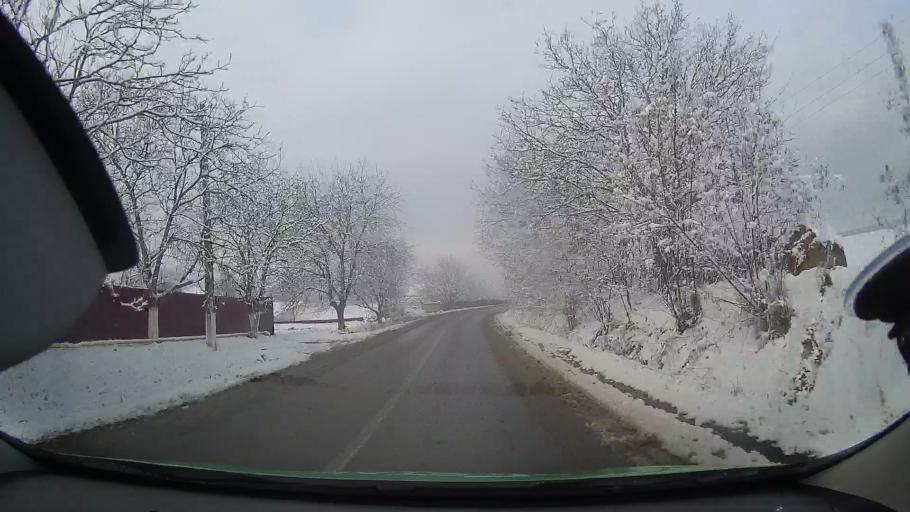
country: RO
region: Mures
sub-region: Comuna Atintis
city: Atintis
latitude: 46.4435
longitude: 24.0909
